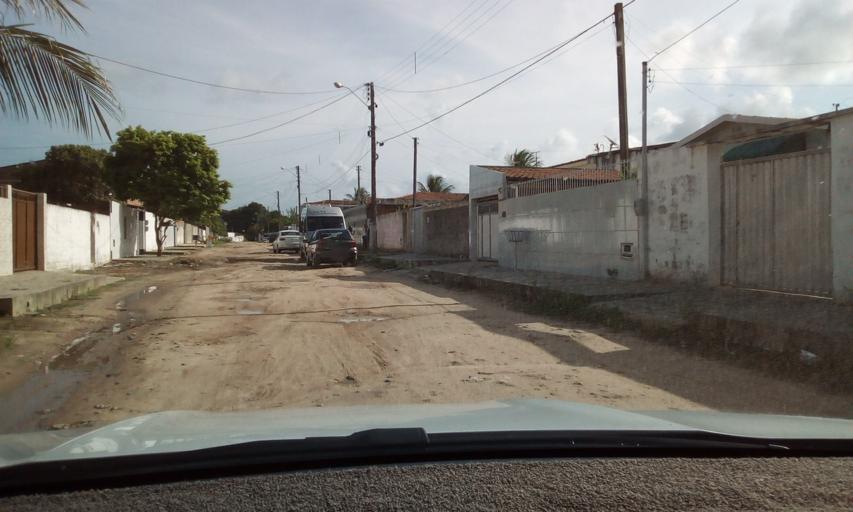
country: BR
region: Paraiba
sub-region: Joao Pessoa
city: Joao Pessoa
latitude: -7.1826
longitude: -34.8245
